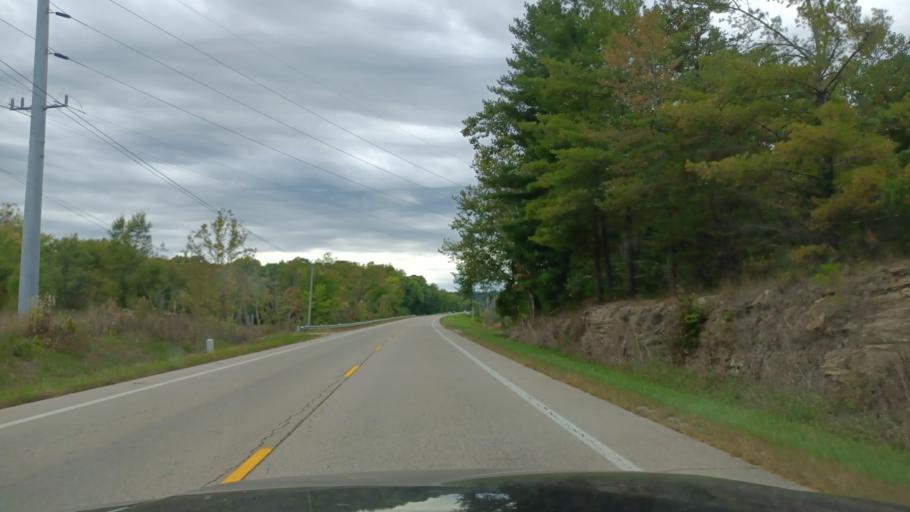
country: US
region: Ohio
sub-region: Vinton County
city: McArthur
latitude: 39.2354
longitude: -82.4198
